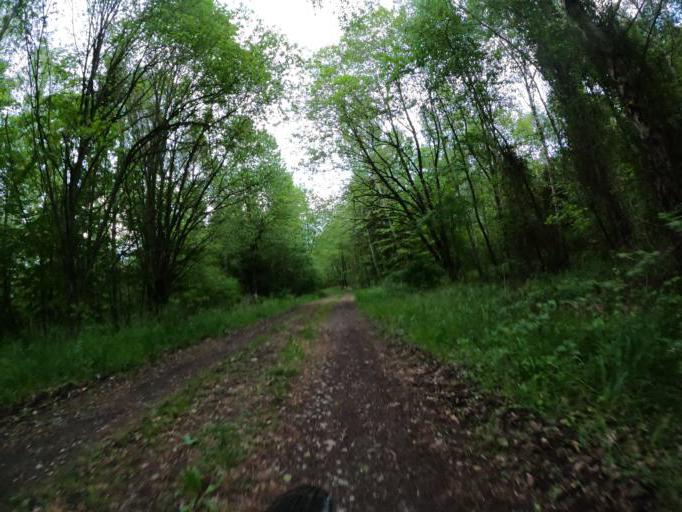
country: DE
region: Baden-Wuerttemberg
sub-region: Regierungsbezirk Stuttgart
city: Aidlingen
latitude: 48.6946
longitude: 8.9194
